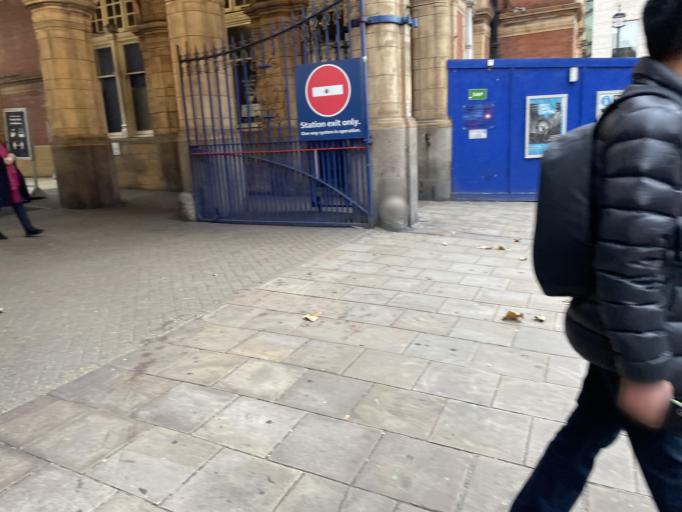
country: GB
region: England
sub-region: Greater London
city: Bayswater
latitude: 51.5228
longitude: -0.1632
